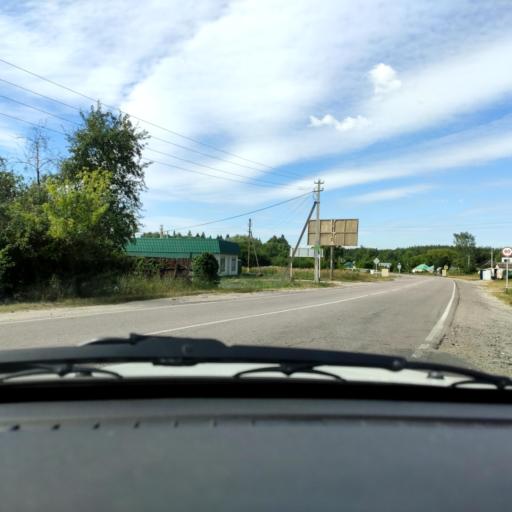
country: RU
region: Voronezj
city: Uglyanets
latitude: 51.8595
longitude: 39.6734
